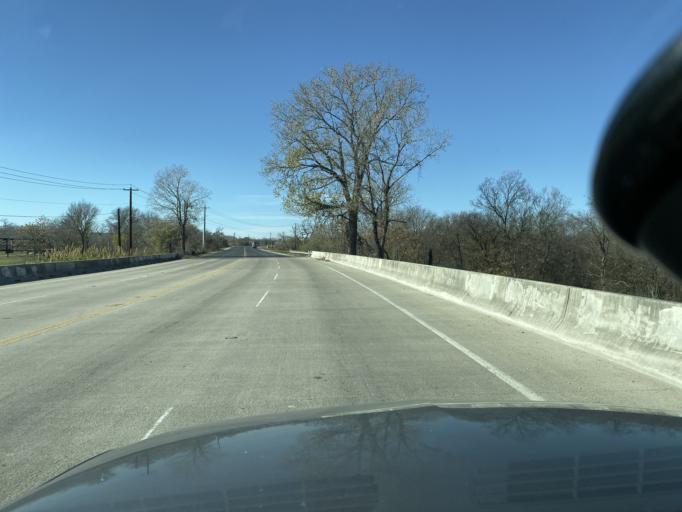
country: US
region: Texas
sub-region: Travis County
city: Garfield
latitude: 30.1698
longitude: -97.6621
